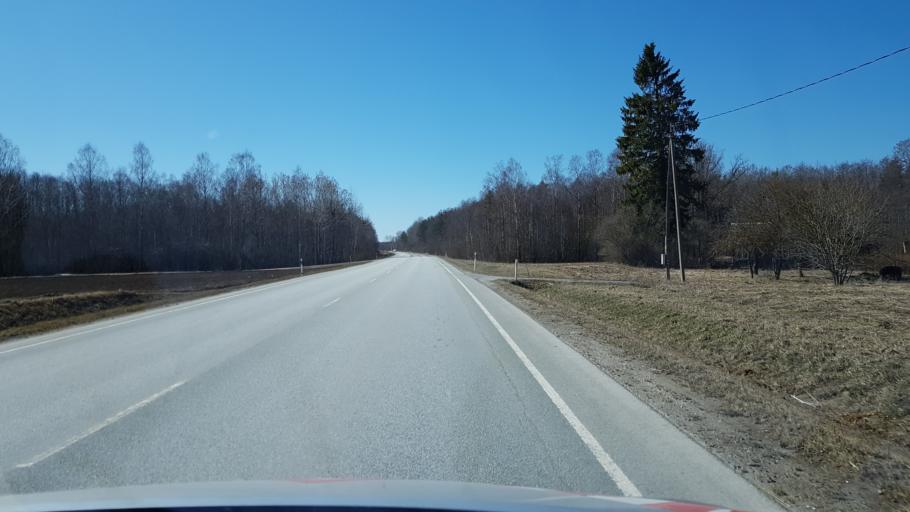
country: EE
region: Laeaene-Virumaa
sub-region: Someru vald
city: Someru
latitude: 59.4541
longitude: 26.4381
